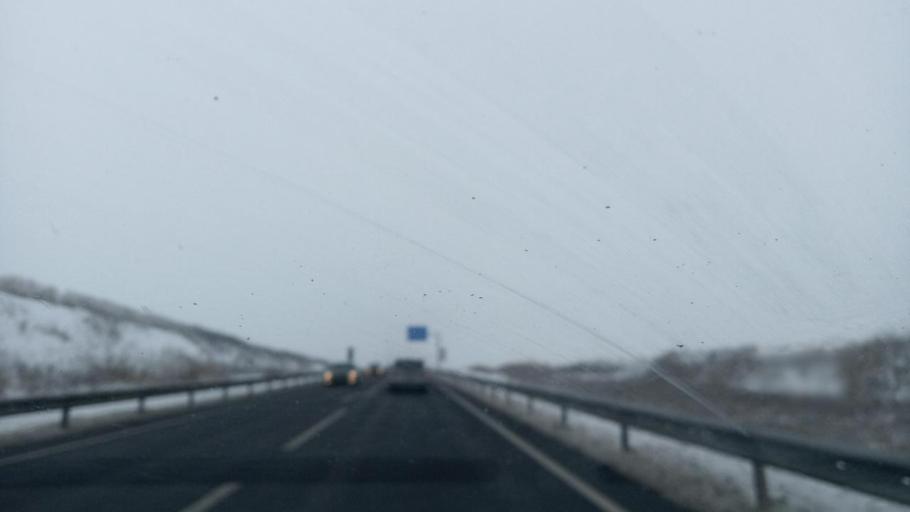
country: RO
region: Bacau
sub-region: Comuna Saucesti
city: Saucesti
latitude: 46.6369
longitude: 26.9187
